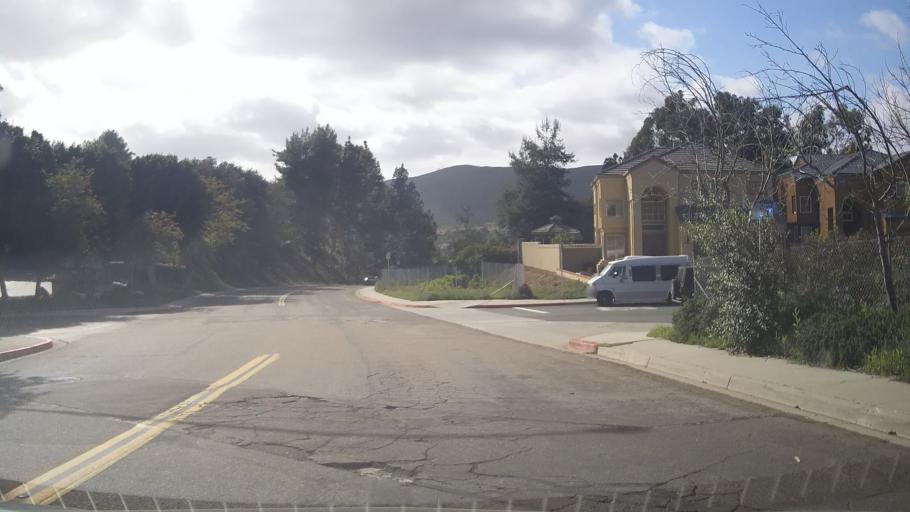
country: US
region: California
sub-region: San Diego County
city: Poway
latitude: 32.9705
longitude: -117.0828
